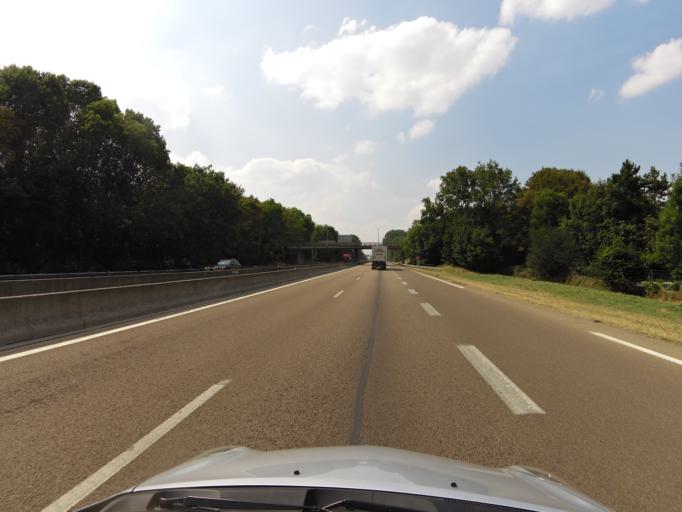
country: FR
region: Champagne-Ardenne
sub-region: Departement de la Marne
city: Reims
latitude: 49.2534
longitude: 4.0130
